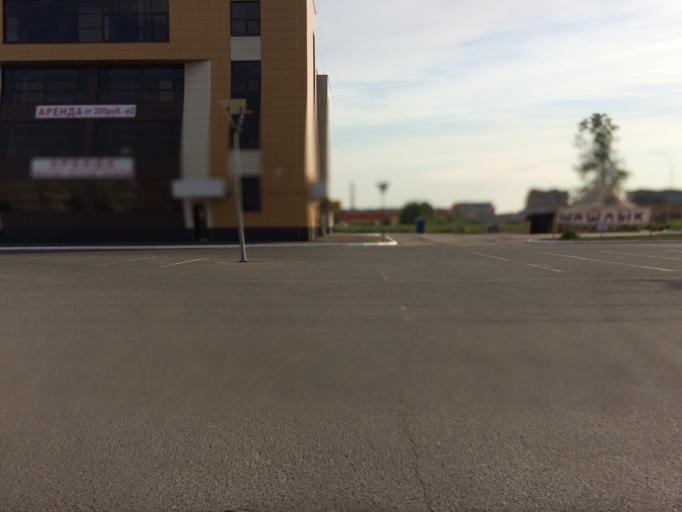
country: RU
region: Mariy-El
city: Yoshkar-Ola
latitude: 56.6288
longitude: 47.9294
